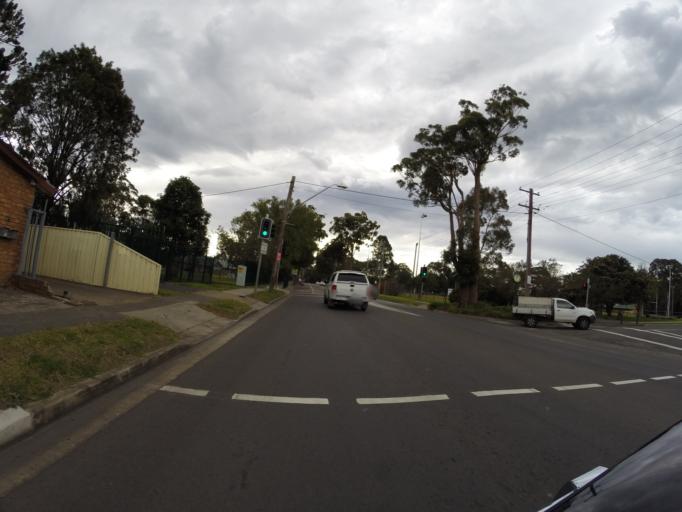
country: AU
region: New South Wales
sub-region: Wollondilly
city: Douglas Park
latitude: -34.1997
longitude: 150.7879
